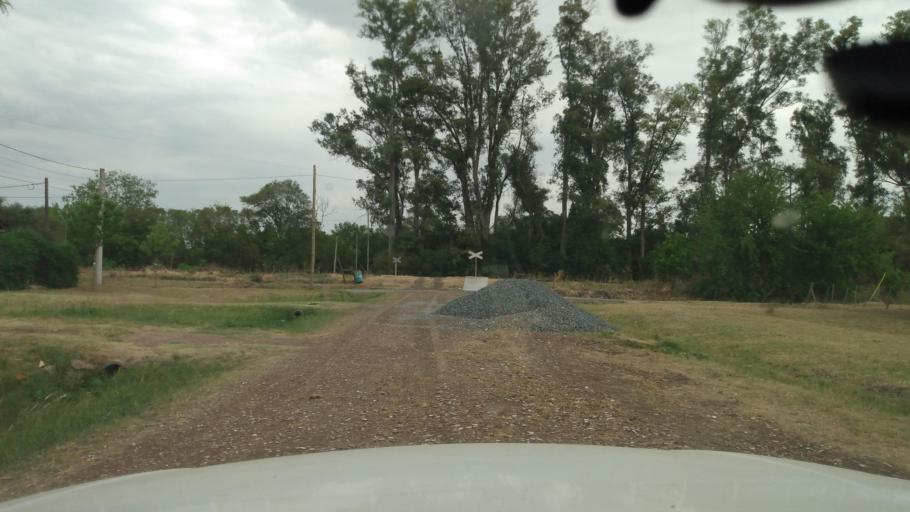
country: AR
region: Buenos Aires
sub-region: Partido de Lujan
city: Lujan
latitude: -34.5533
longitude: -59.2009
